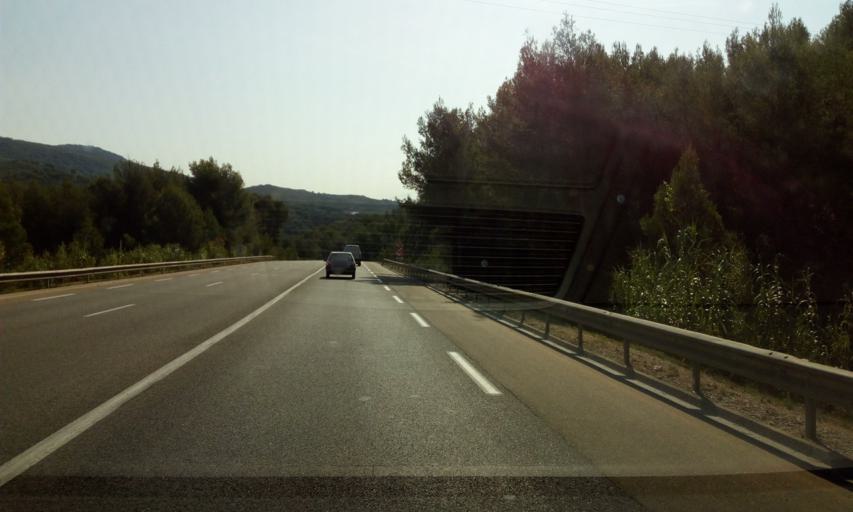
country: FR
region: Provence-Alpes-Cote d'Azur
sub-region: Departement du Var
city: Bandol
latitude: 43.1497
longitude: 5.7555
